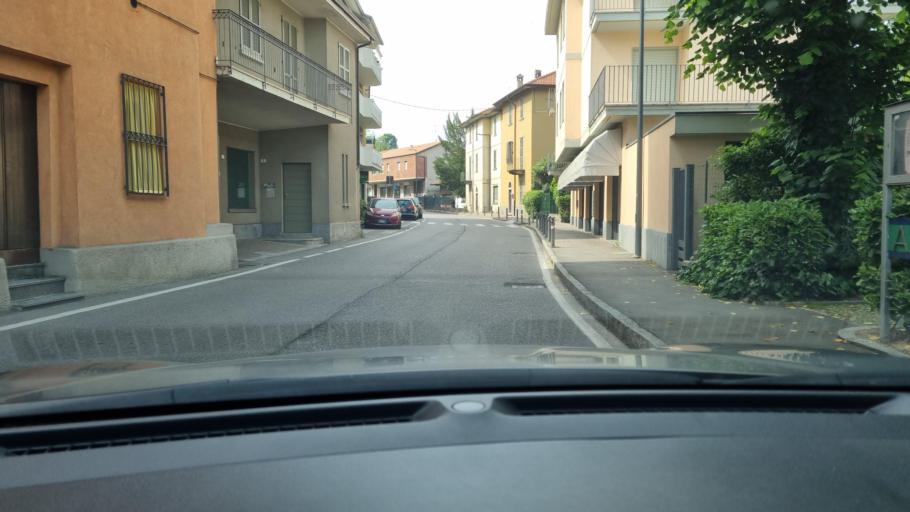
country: IT
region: Lombardy
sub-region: Provincia di Bergamo
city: Mapello
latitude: 45.7095
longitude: 9.5501
